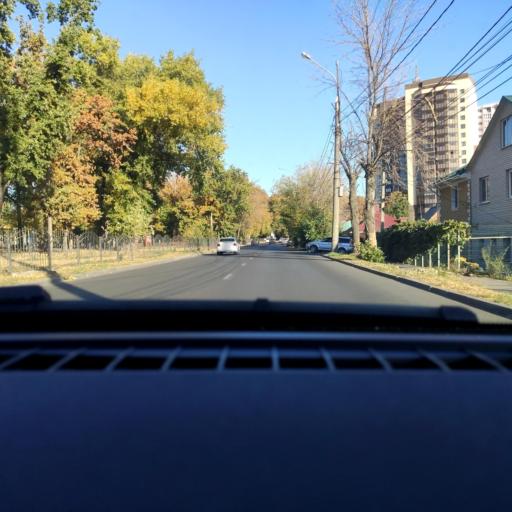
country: RU
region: Voronezj
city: Voronezh
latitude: 51.7071
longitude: 39.2306
